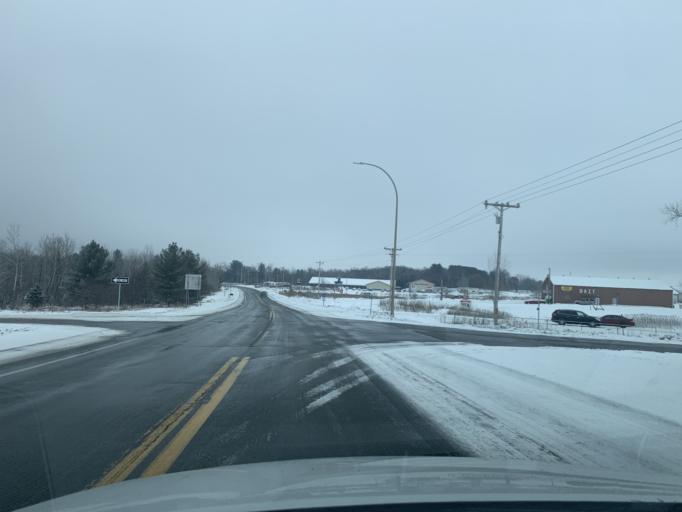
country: US
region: Minnesota
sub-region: Chisago County
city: Harris
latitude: 45.5779
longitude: -92.9916
